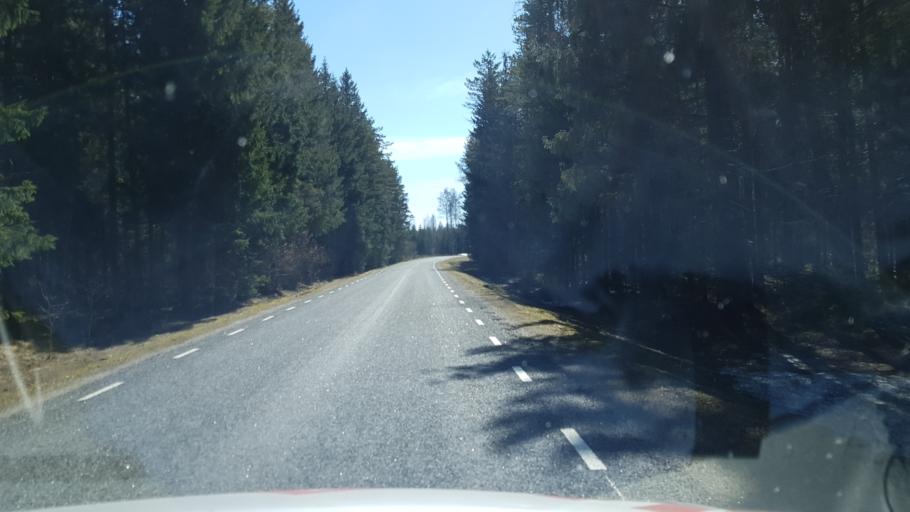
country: EE
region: Laeaene-Virumaa
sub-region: Vinni vald
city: Vinni
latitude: 59.1411
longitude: 26.5242
